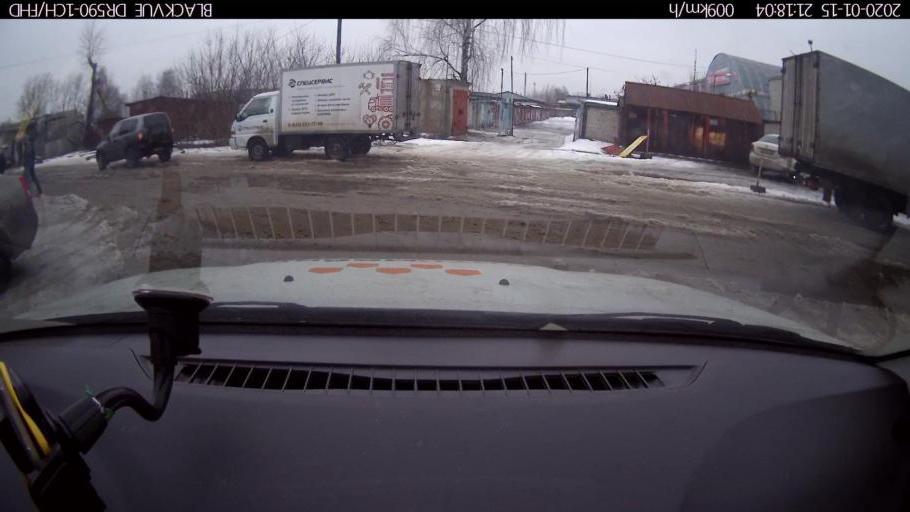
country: RU
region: Nizjnij Novgorod
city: Gorbatovka
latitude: 56.3004
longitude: 43.8613
